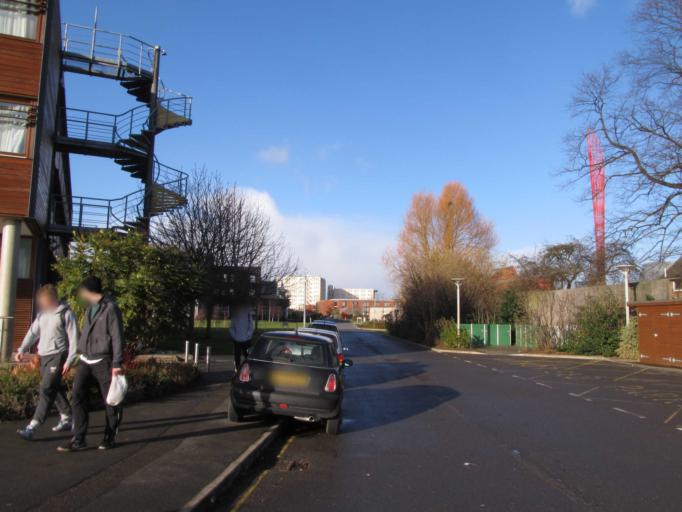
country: GB
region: England
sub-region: Nottingham
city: Nottingham
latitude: 52.9499
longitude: -1.1854
